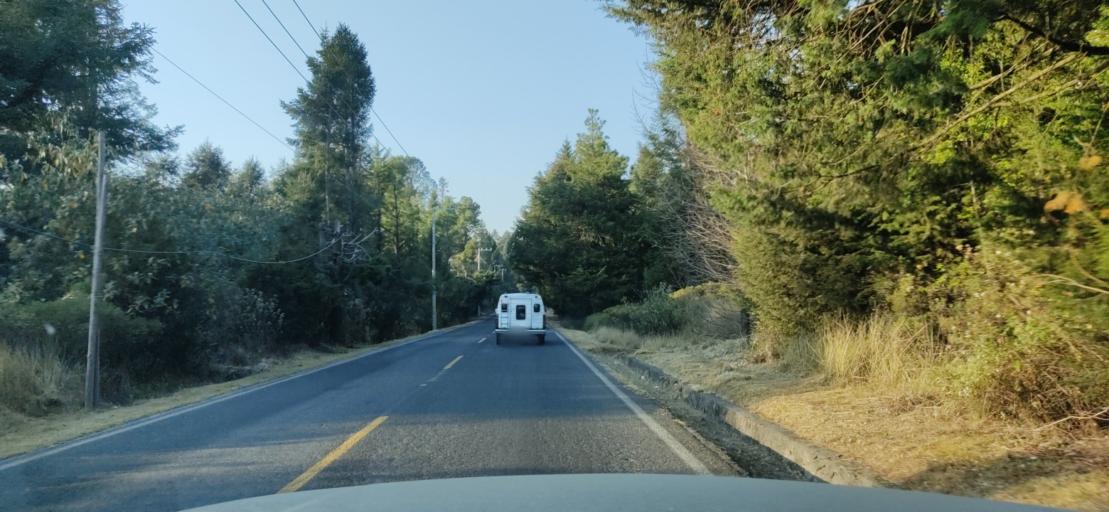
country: MX
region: Mexico
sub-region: Ocoyoacac
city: San Jeronimo Acazulco
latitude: 19.2550
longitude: -99.3780
